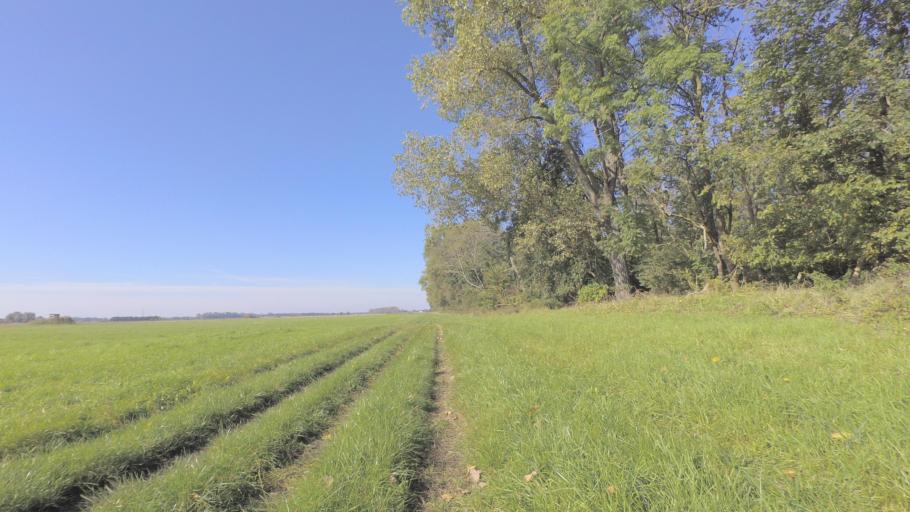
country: DE
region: Brandenburg
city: Rangsdorf
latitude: 52.2949
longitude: 13.3688
